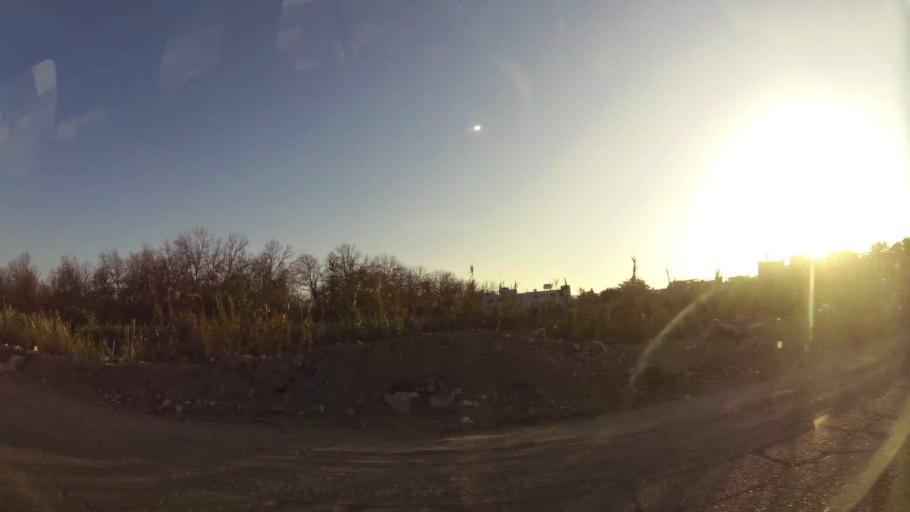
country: PE
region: Ica
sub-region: Provincia de Ica
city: Ica
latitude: -14.0798
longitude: -75.7185
